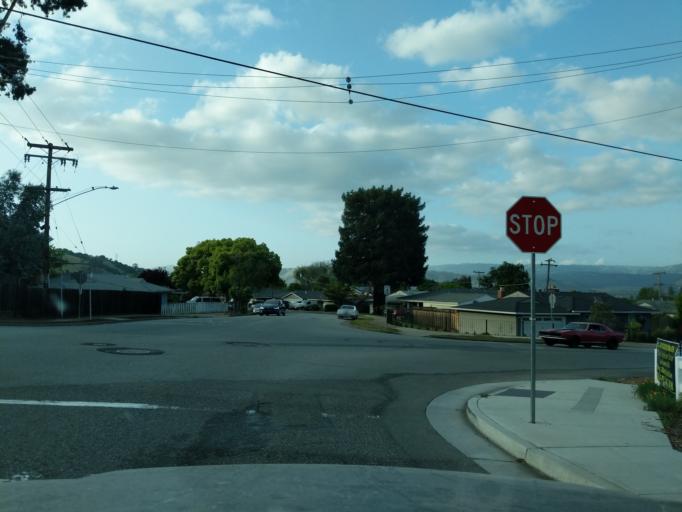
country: US
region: California
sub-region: Santa Clara County
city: Morgan Hill
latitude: 37.1214
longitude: -121.6619
